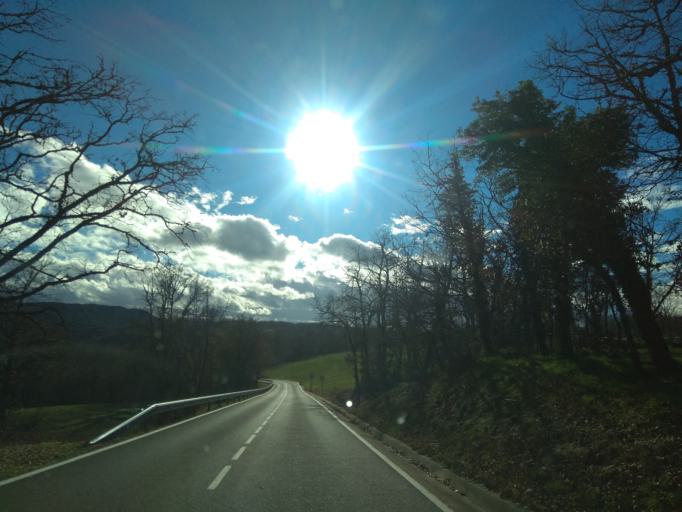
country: ES
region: Cantabria
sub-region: Provincia de Cantabria
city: San Martin de Elines
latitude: 42.9054
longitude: -3.8679
